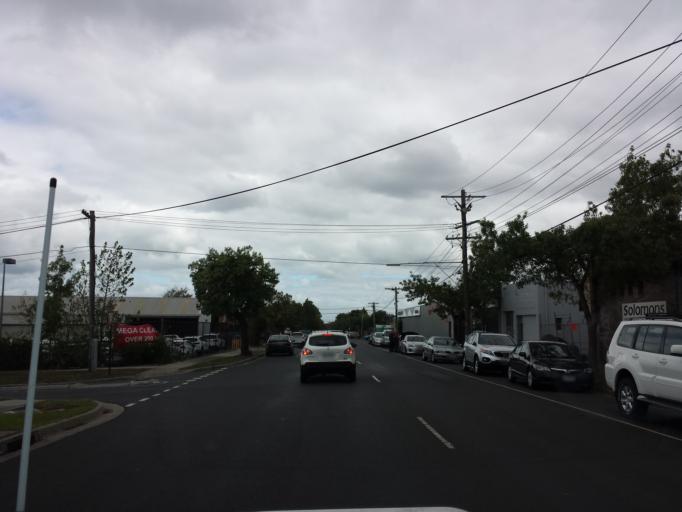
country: AU
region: Victoria
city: Hughesdale
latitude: -37.8926
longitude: 145.0843
